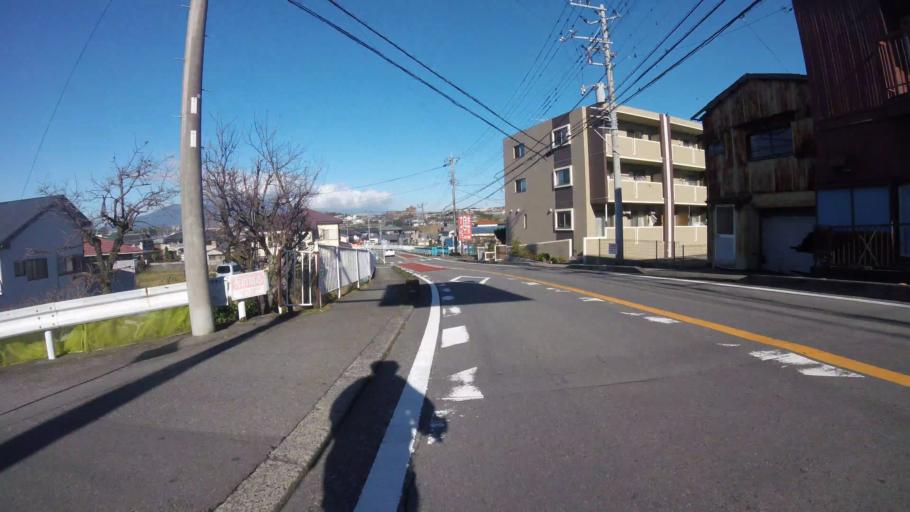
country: JP
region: Shizuoka
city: Mishima
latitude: 35.1217
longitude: 138.9301
